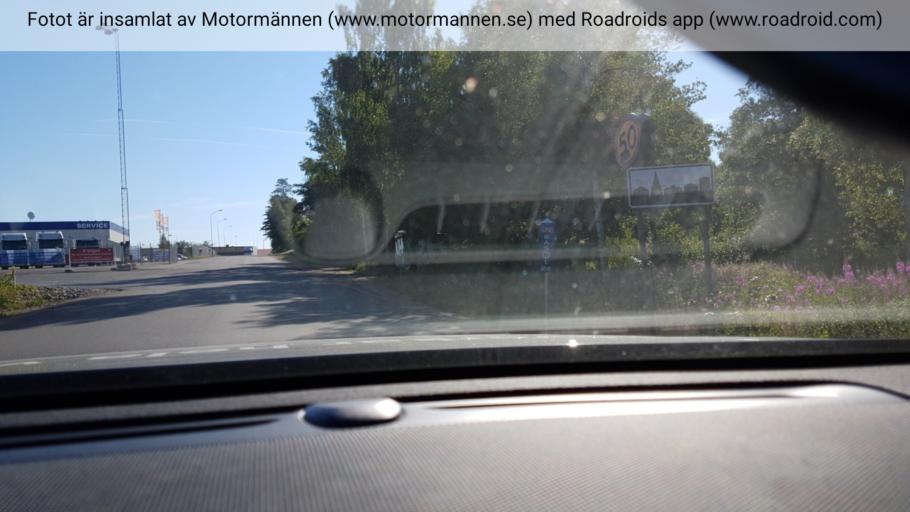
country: SE
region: Kronoberg
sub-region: Markaryds Kommun
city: Markaryd
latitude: 56.4450
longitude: 13.6027
